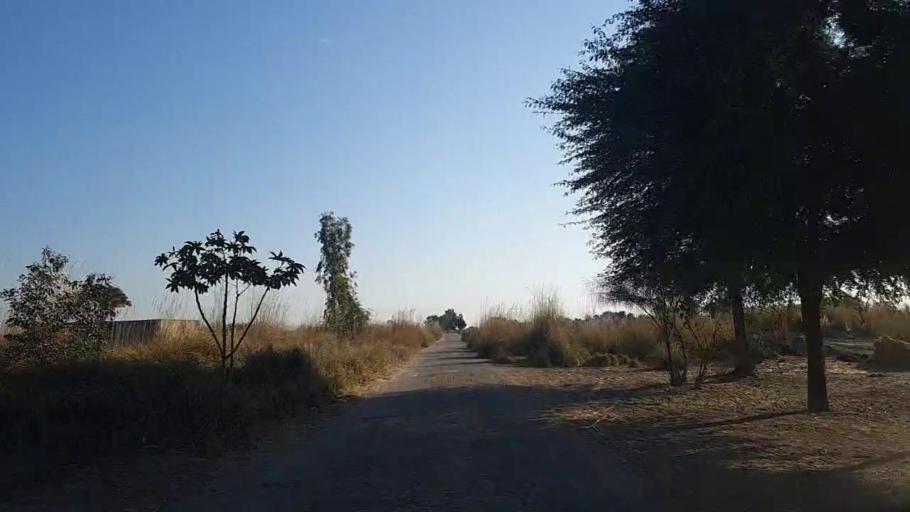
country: PK
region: Sindh
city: Khadro
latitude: 26.2773
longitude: 68.8603
